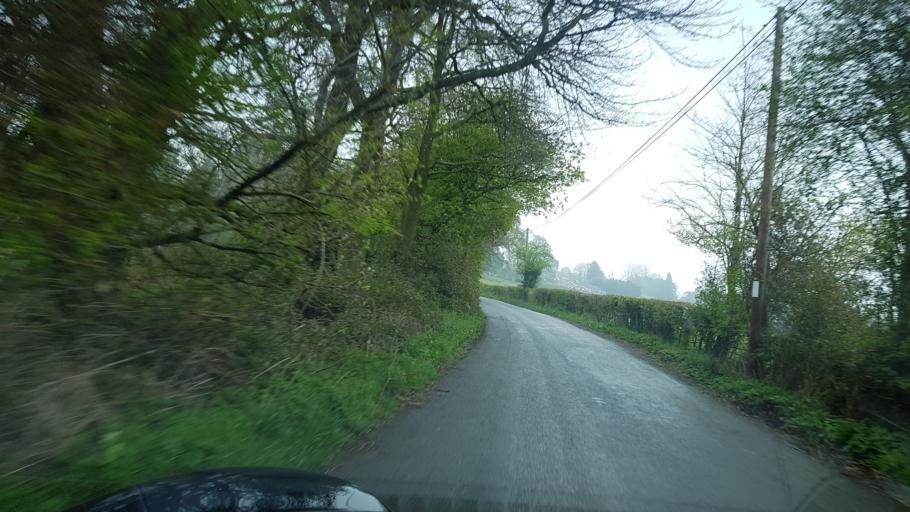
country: GB
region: England
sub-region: Herefordshire
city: Brockhampton
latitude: 52.0151
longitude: -2.5704
